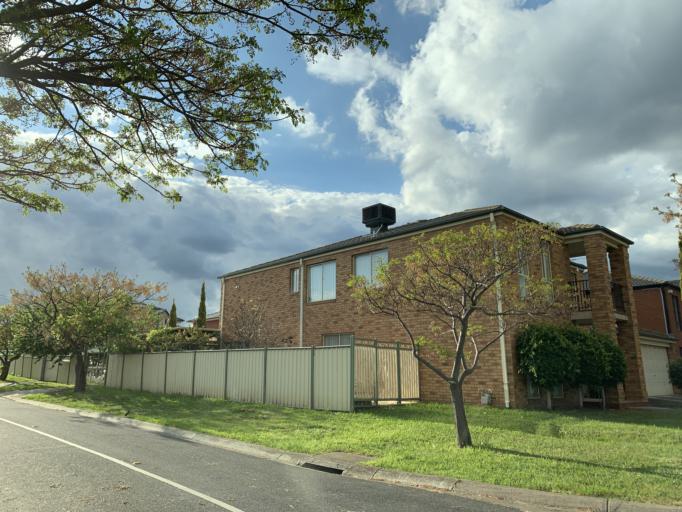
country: AU
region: Victoria
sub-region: Brimbank
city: Albion
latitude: -37.7678
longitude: 144.8454
